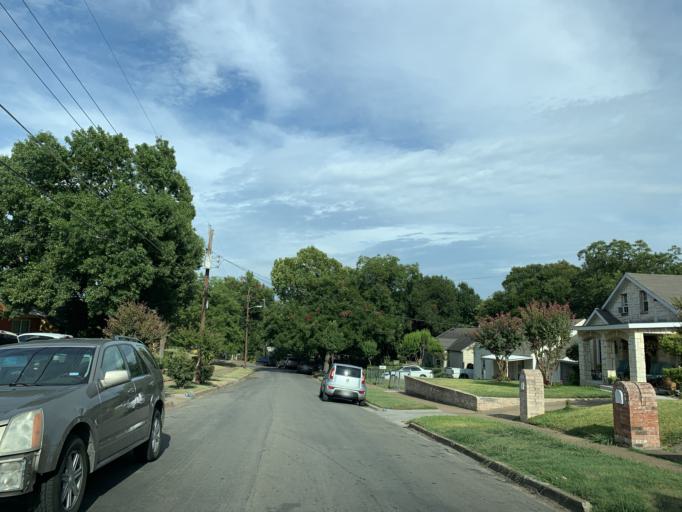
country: US
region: Texas
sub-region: Dallas County
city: Cockrell Hill
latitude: 32.7345
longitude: -96.8351
